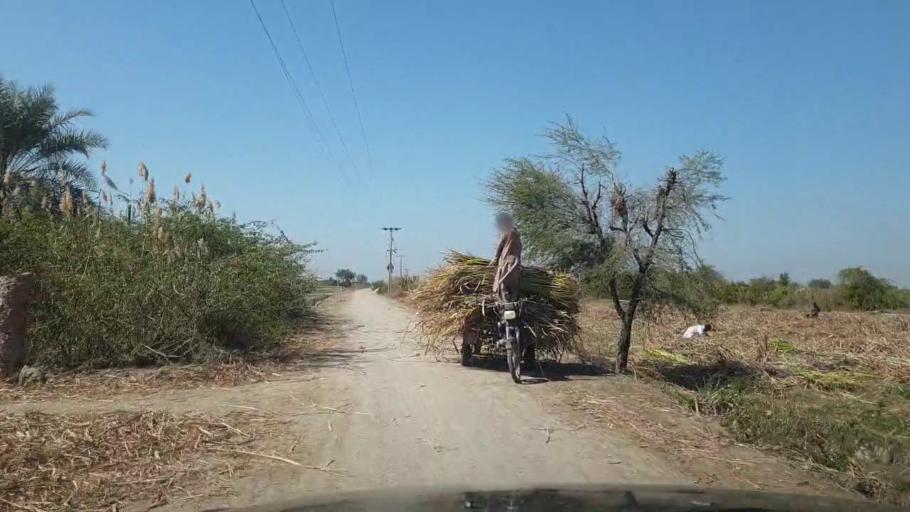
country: PK
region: Sindh
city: Mirpur Khas
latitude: 25.5978
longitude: 69.0677
